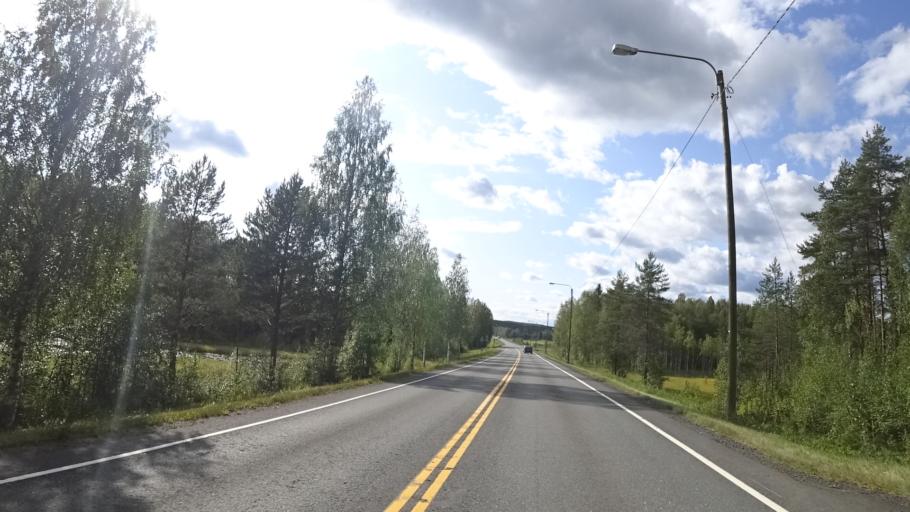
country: FI
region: North Karelia
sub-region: Keski-Karjala
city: Tohmajaervi
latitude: 62.2204
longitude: 30.3999
